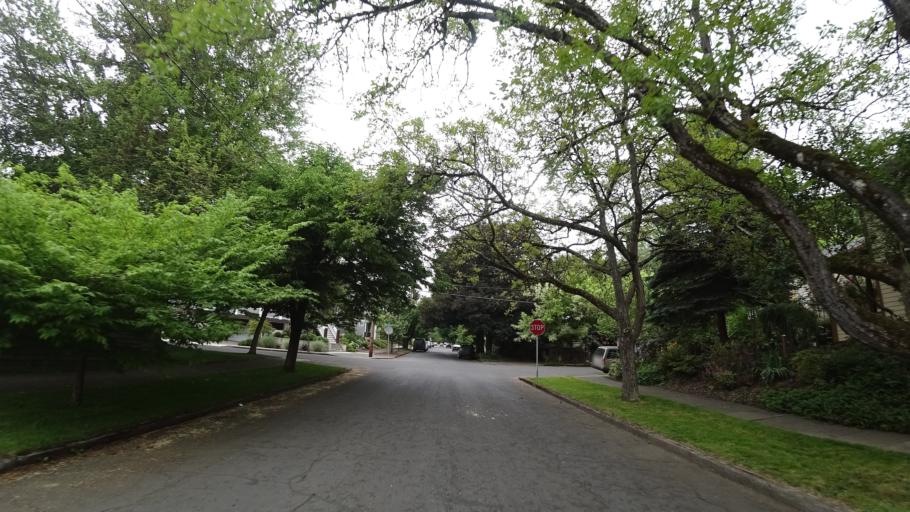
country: US
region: Oregon
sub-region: Clackamas County
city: Milwaukie
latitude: 45.4626
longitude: -122.6570
